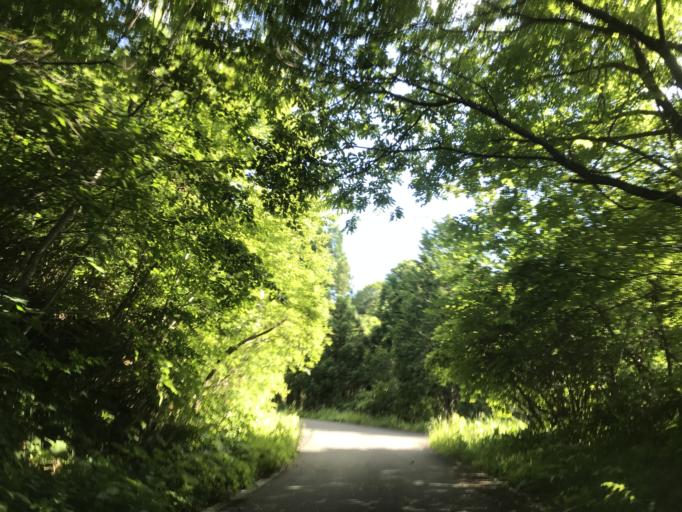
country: JP
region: Iwate
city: Ichinoseki
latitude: 38.8927
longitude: 140.9067
